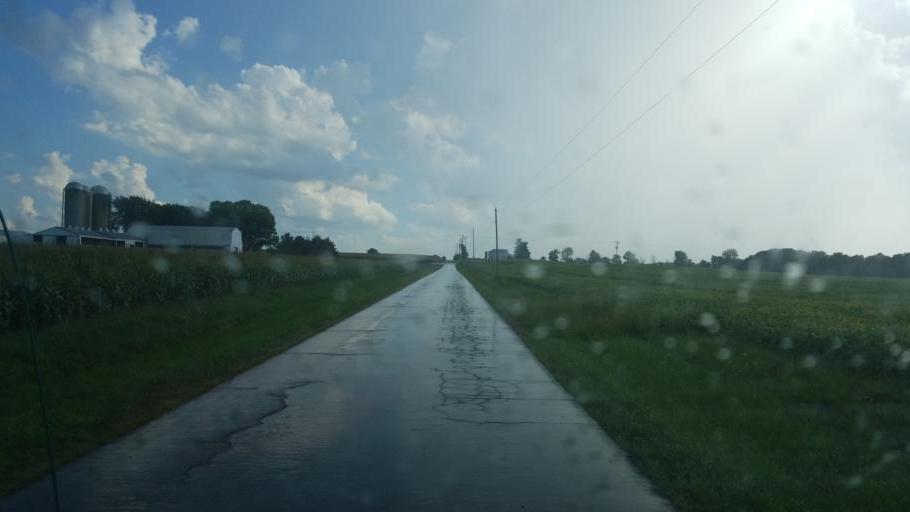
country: US
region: Ohio
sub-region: Huron County
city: Greenwich
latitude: 40.9968
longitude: -82.5585
